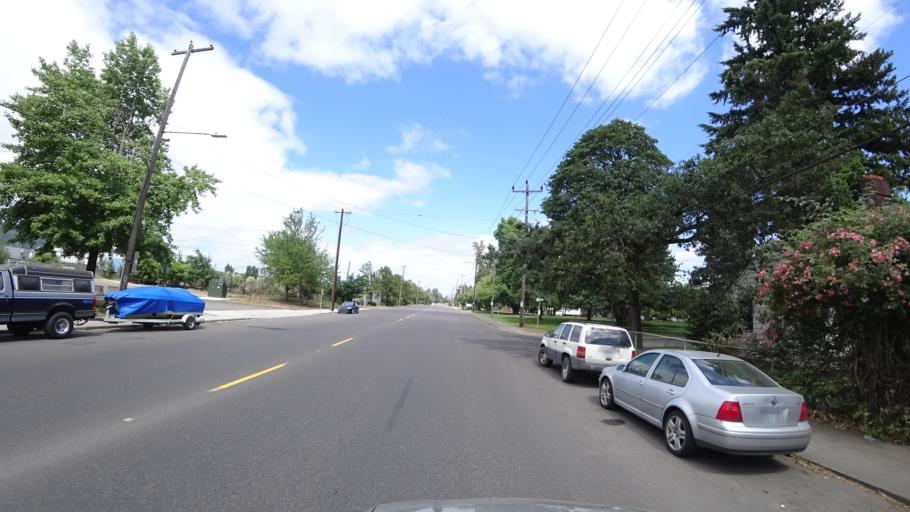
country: US
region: Oregon
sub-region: Washington County
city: West Haven
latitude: 45.6010
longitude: -122.7630
